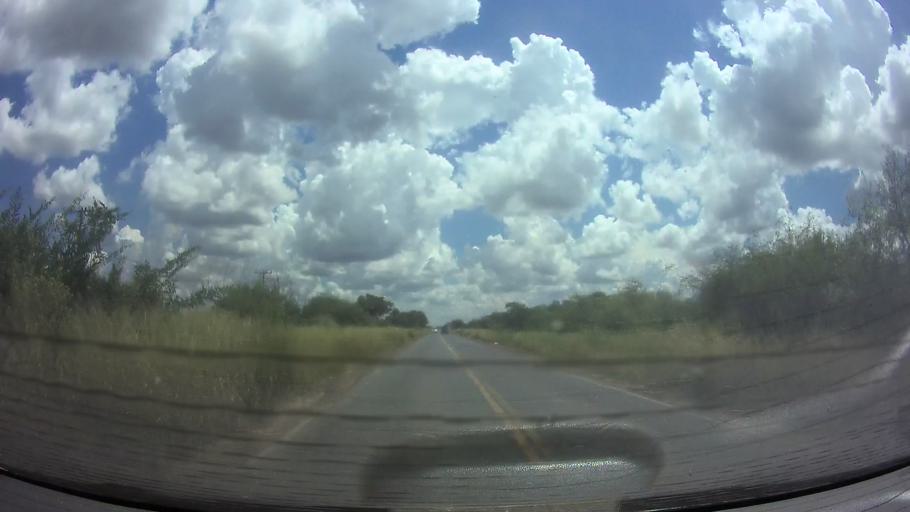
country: PY
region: Central
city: Colonia Mariano Roque Alonso
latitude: -25.1879
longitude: -57.6001
